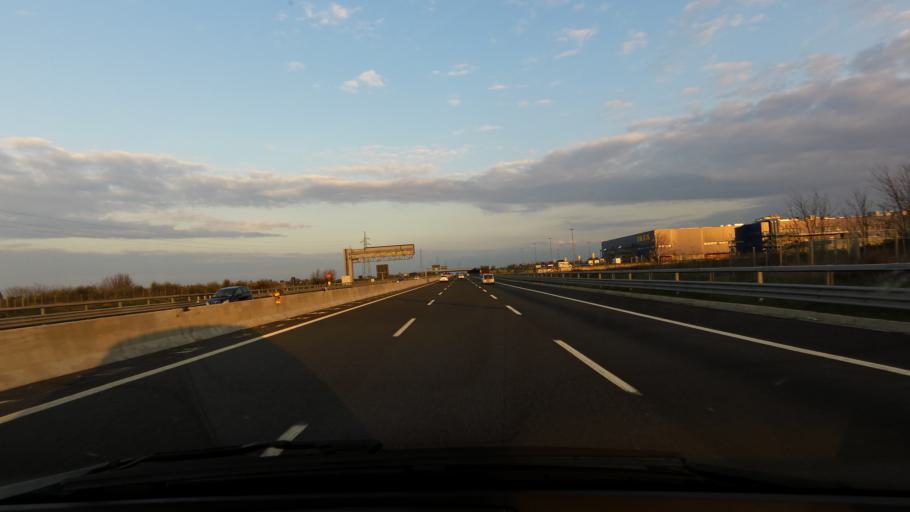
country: IT
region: Emilia-Romagna
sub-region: Provincia di Rimini
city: Santa Giustina
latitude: 44.0818
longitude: 12.4731
